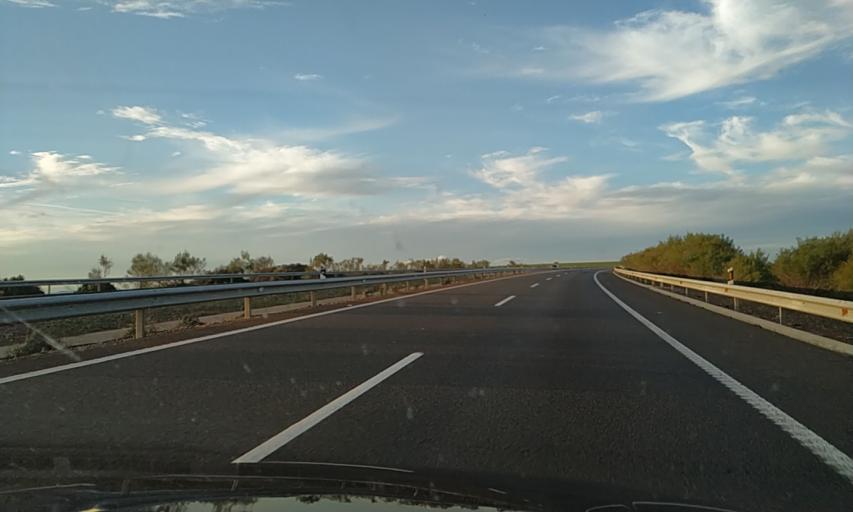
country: ES
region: Extremadura
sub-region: Provincia de Badajoz
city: Merida
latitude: 38.9583
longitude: -6.3433
